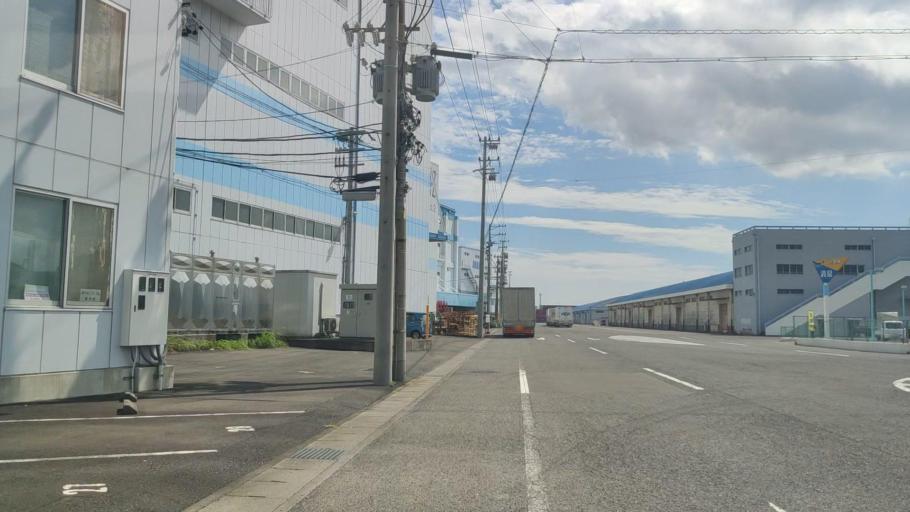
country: JP
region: Shizuoka
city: Shizuoka-shi
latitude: 35.0440
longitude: 138.5139
